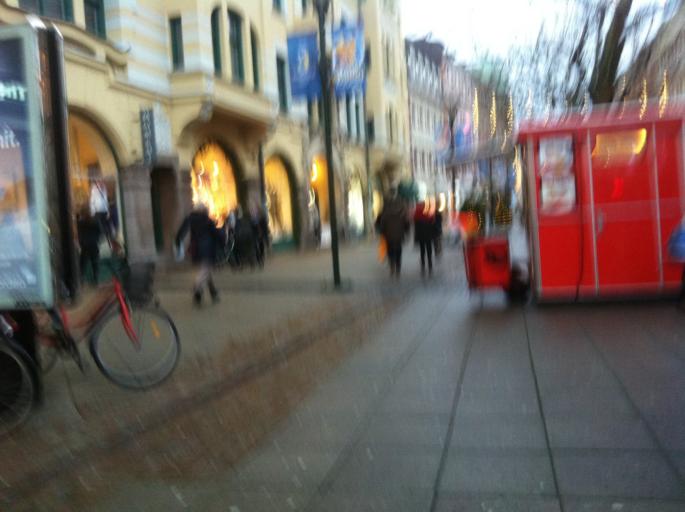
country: SE
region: Skane
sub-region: Malmo
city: Malmoe
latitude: 55.6008
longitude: 13.0011
